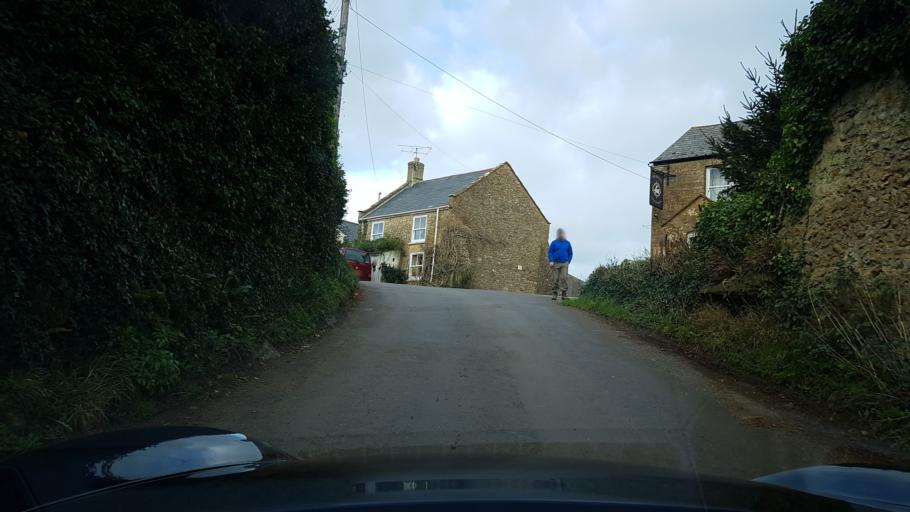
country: GB
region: England
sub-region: Dorset
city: Bridport
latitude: 50.7211
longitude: -2.7157
